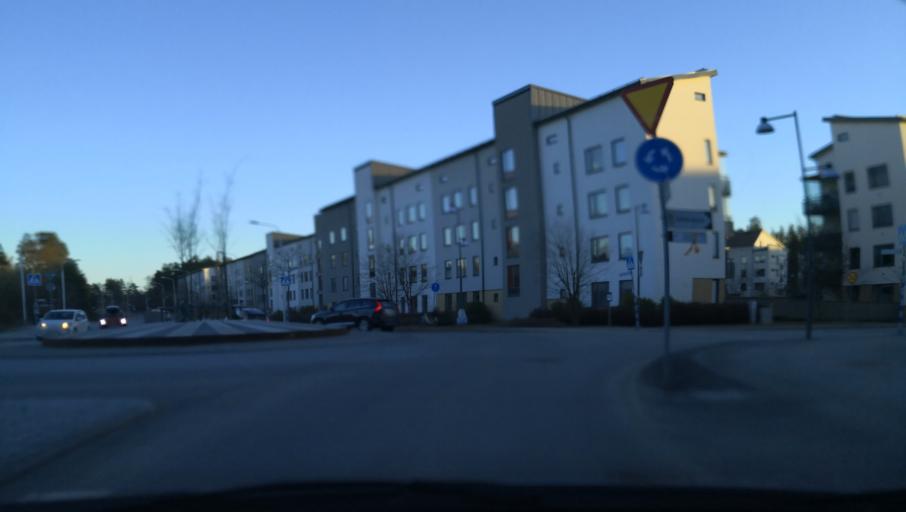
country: SE
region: Stockholm
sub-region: Varmdo Kommun
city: Gustavsberg
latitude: 59.3198
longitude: 18.3877
